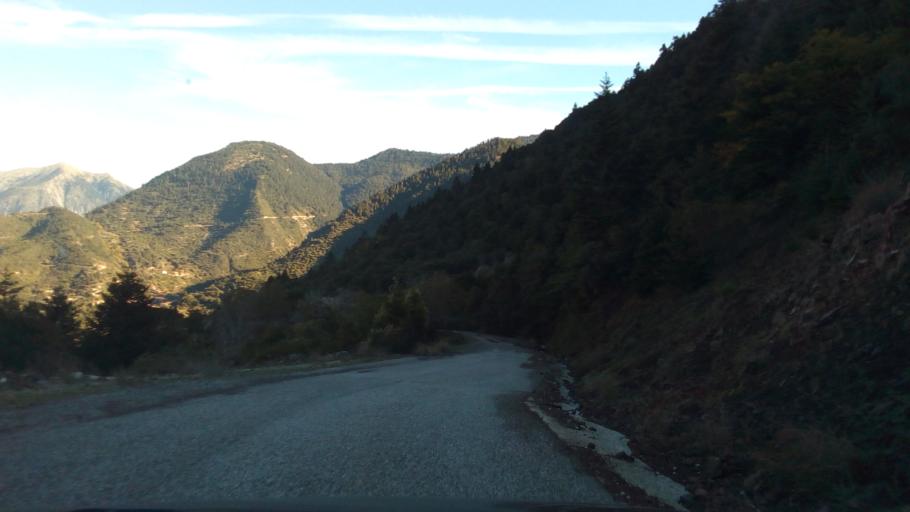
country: GR
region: West Greece
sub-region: Nomos Aitolias kai Akarnanias
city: Nafpaktos
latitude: 38.5468
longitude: 21.8516
